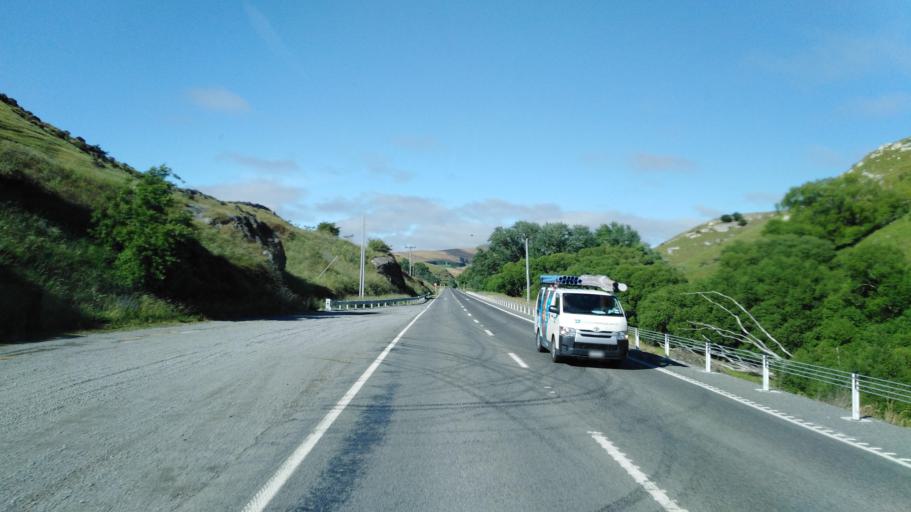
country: NZ
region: Canterbury
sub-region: Hurunui District
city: Amberley
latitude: -43.0005
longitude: 172.7133
